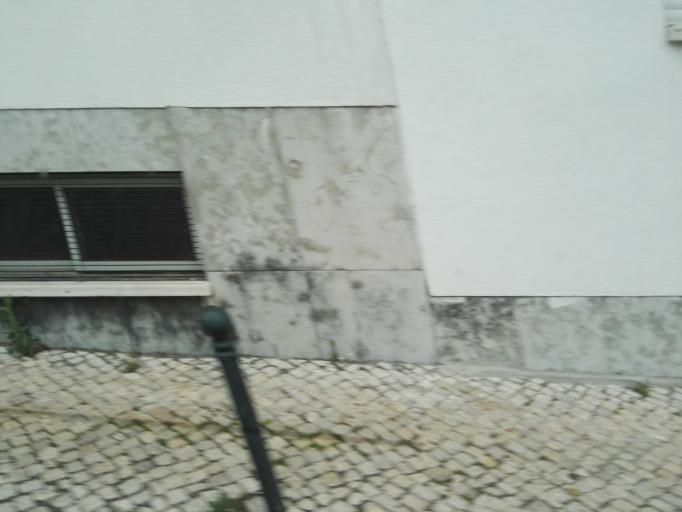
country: PT
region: Lisbon
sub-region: Oeiras
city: Terrugem
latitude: 38.7054
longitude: -9.2749
